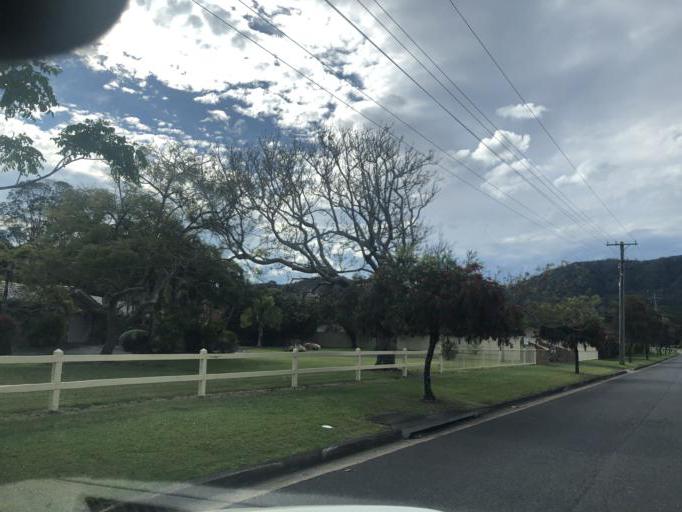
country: AU
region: New South Wales
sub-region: Coffs Harbour
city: Coffs Harbour
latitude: -30.2874
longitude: 153.0973
